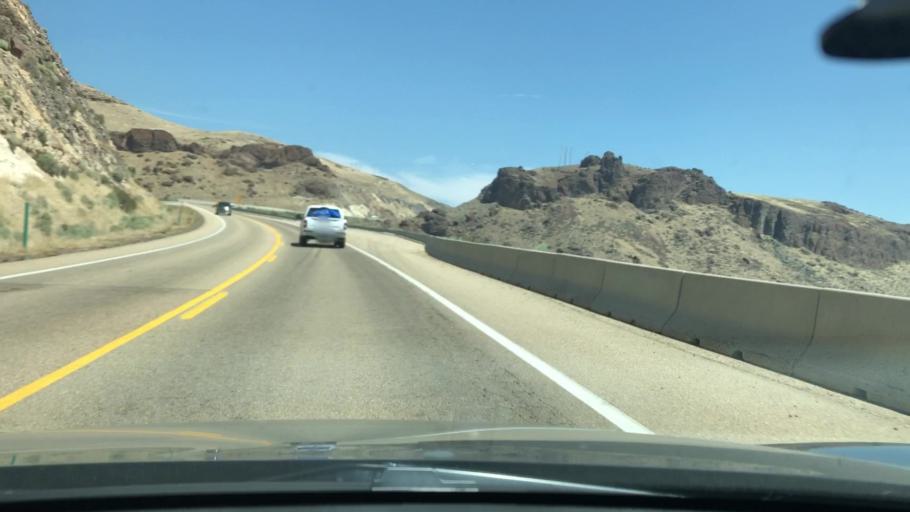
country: US
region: Idaho
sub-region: Owyhee County
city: Marsing
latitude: 43.4005
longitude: -116.8771
